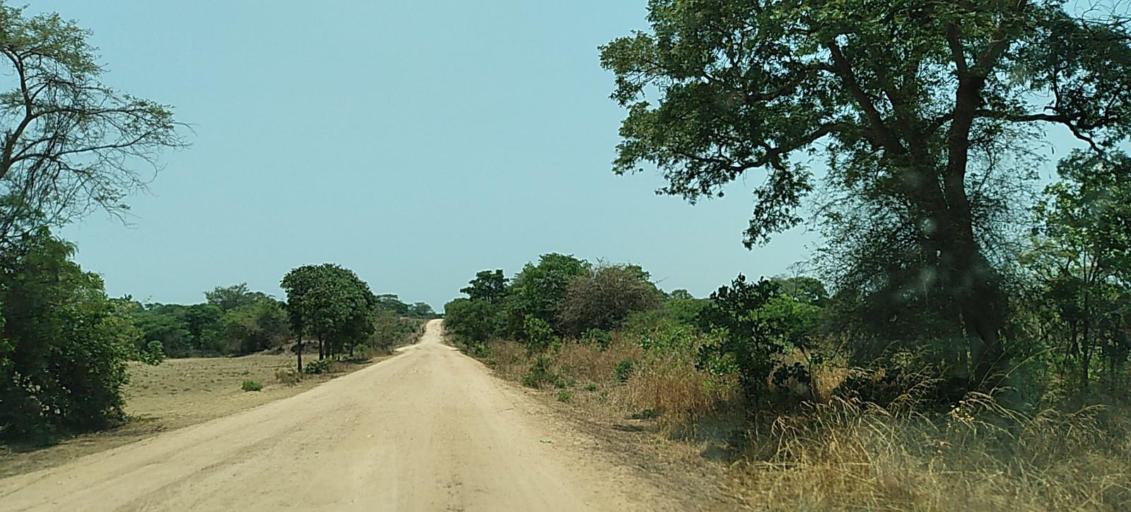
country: ZM
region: Copperbelt
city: Mpongwe
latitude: -13.8152
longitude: 27.8475
